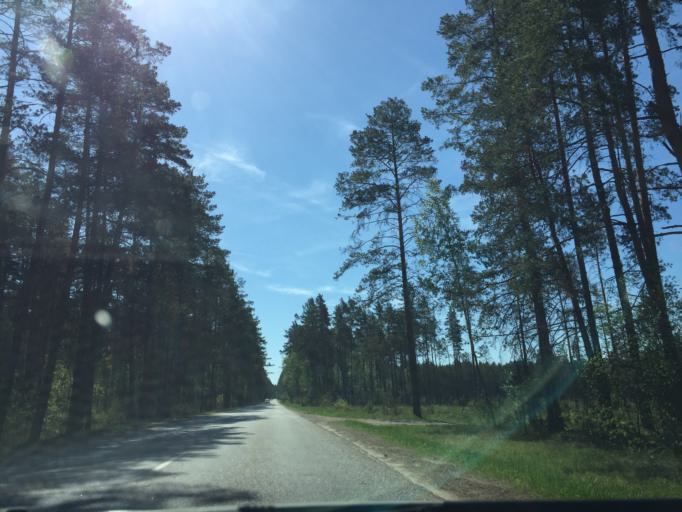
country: LV
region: Garkalne
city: Garkalne
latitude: 57.0328
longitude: 24.4224
